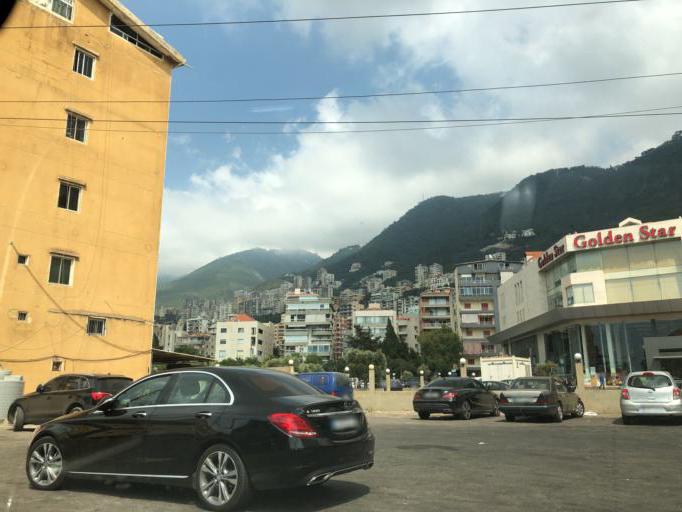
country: LB
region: Mont-Liban
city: Djounie
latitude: 33.9886
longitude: 35.6380
